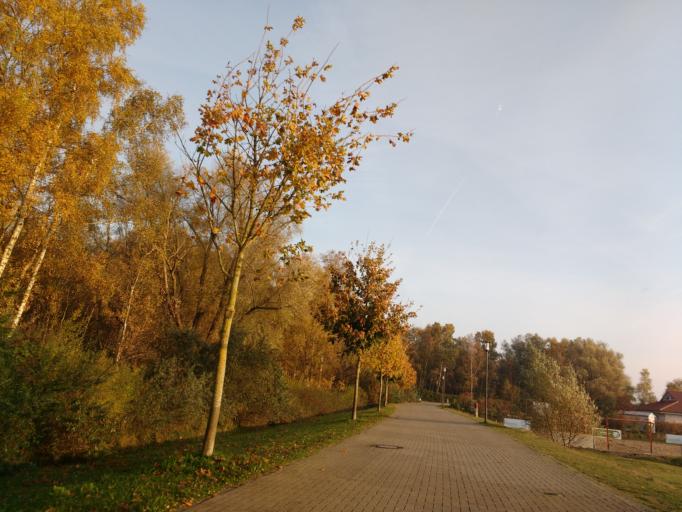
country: DE
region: Mecklenburg-Vorpommern
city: Ostseebad Boltenhagen
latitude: 53.9767
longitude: 11.2536
